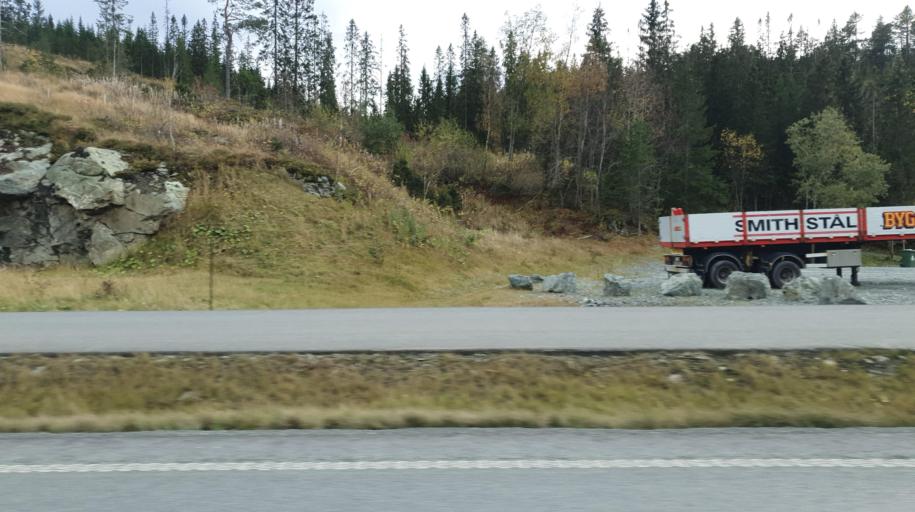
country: NO
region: Sor-Trondelag
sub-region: Klaebu
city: Klaebu
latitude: 63.3177
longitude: 10.4051
